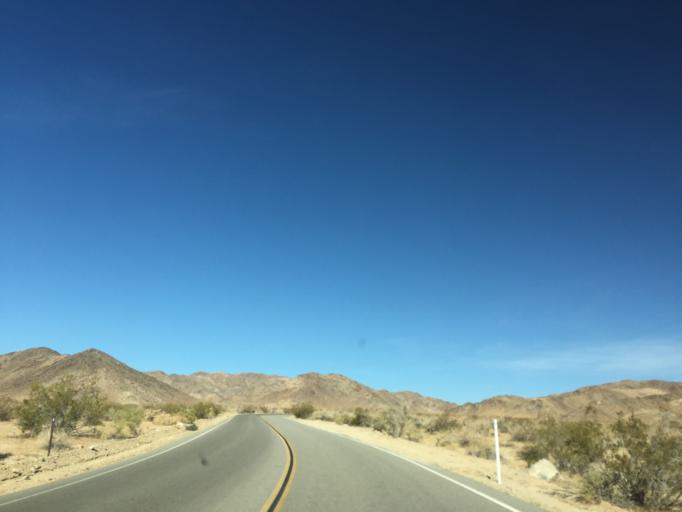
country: US
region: California
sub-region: San Bernardino County
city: Twentynine Palms
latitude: 33.9297
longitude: -115.9444
